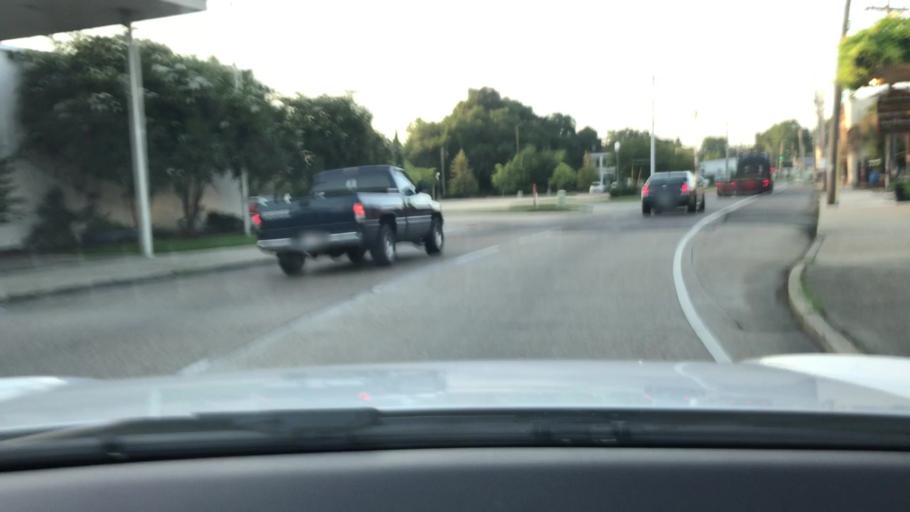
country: US
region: Louisiana
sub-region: Iberville Parish
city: Plaquemine
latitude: 30.2912
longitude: -91.2357
